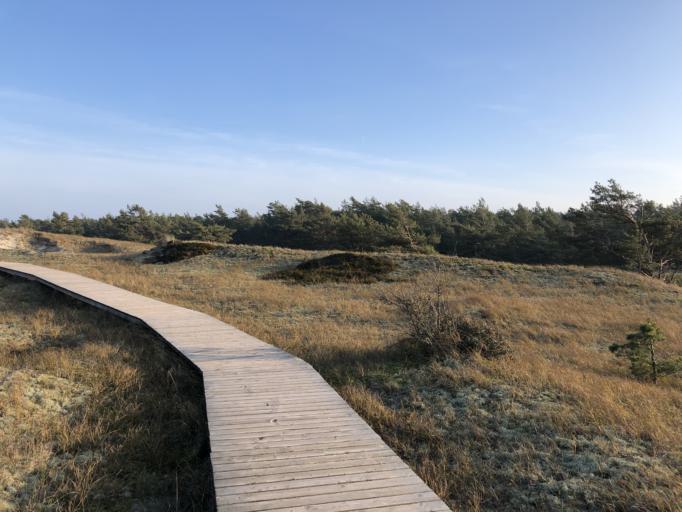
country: DE
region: Mecklenburg-Vorpommern
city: Ostseebad Prerow
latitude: 54.4787
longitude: 12.5077
